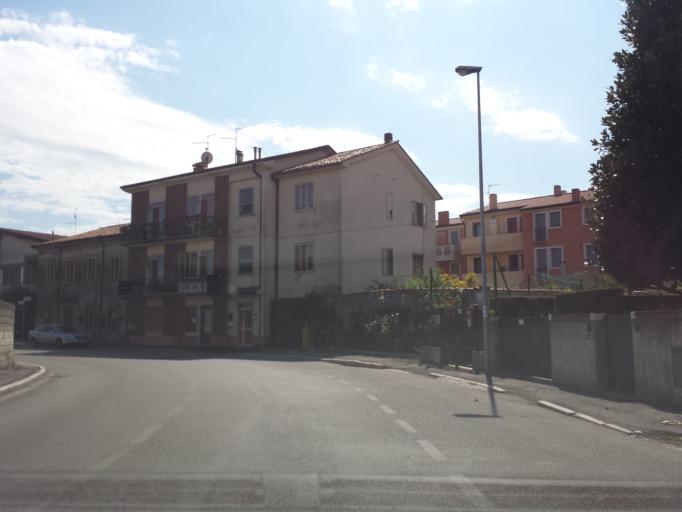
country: IT
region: Veneto
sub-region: Provincia di Verona
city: San Bonifacio
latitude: 45.3967
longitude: 11.2648
